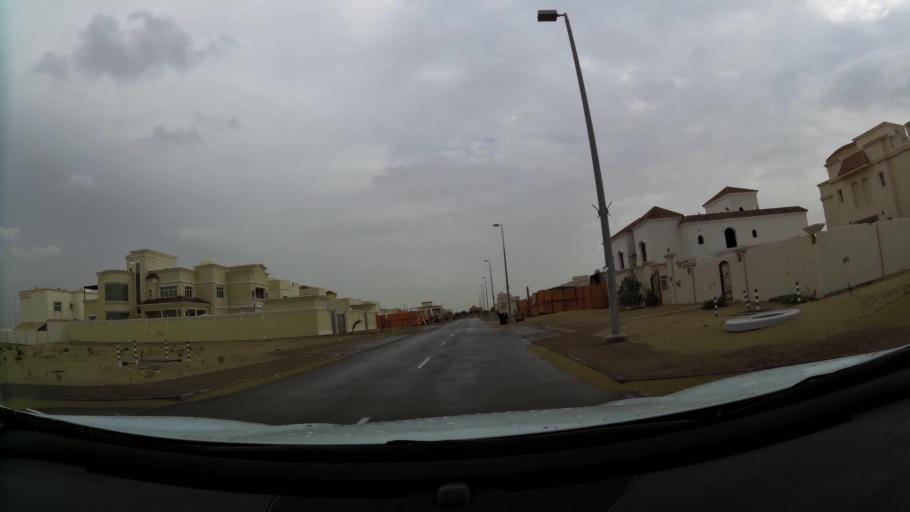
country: AE
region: Abu Dhabi
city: Abu Dhabi
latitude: 24.3670
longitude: 54.6240
